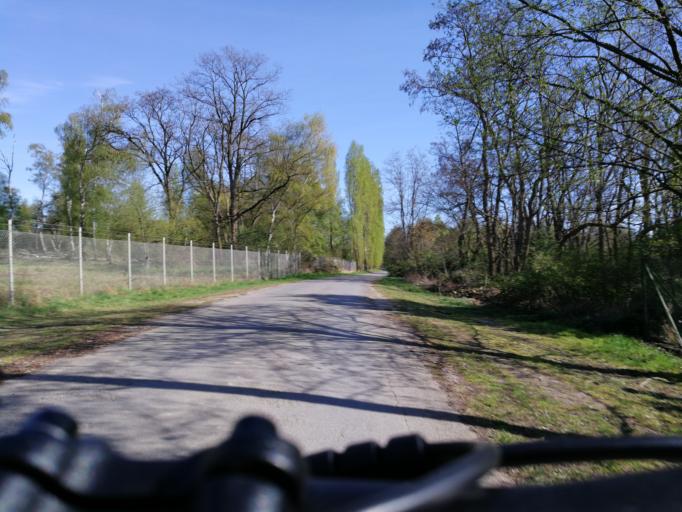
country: DE
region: North Rhine-Westphalia
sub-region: Regierungsbezirk Dusseldorf
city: Dormagen
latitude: 51.1426
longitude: 6.7832
